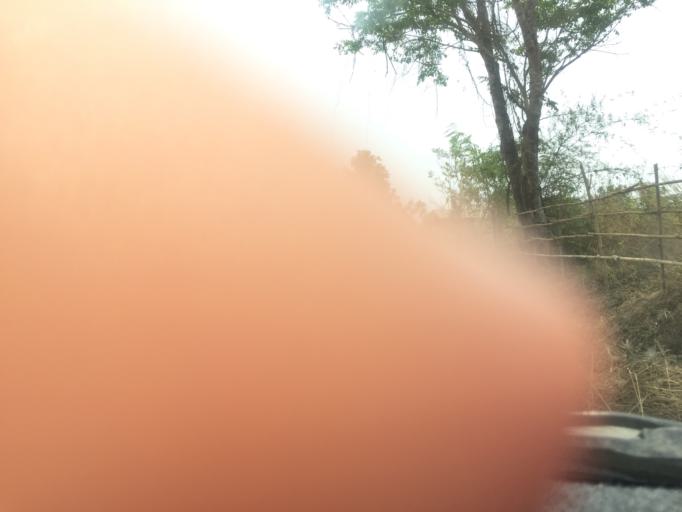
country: LA
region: Xiagnabouli
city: Muang Kenthao
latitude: 17.7862
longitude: 101.2456
